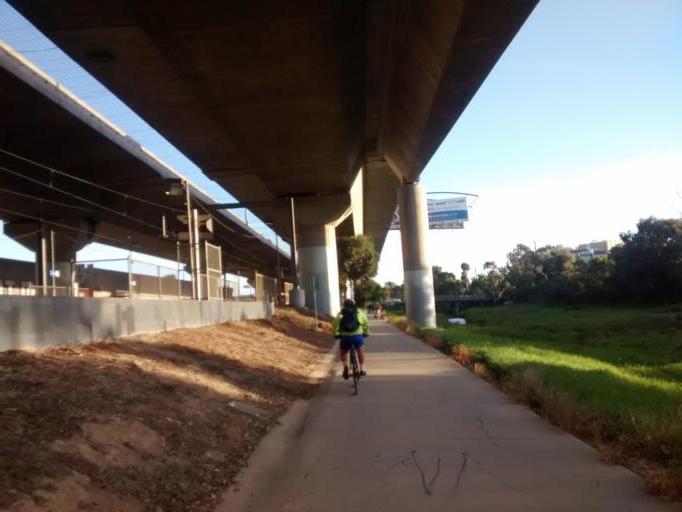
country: AU
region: Victoria
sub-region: Moonee Valley
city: Flemington
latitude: -37.7933
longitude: 144.9362
